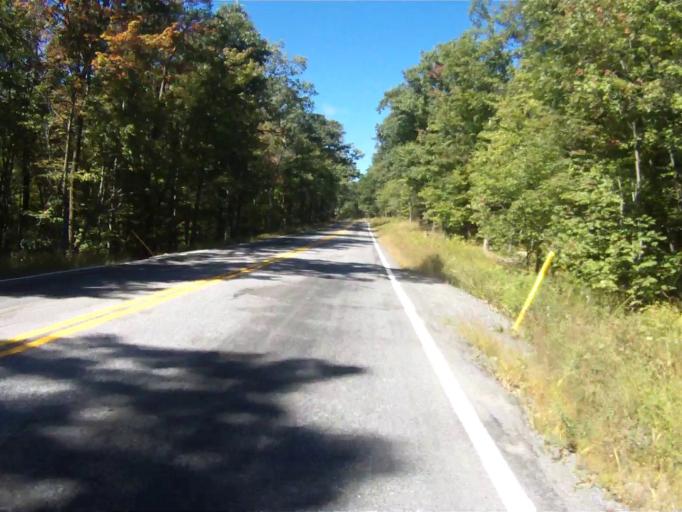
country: US
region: Pennsylvania
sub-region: Centre County
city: Park Forest Village
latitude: 40.9224
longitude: -77.9524
